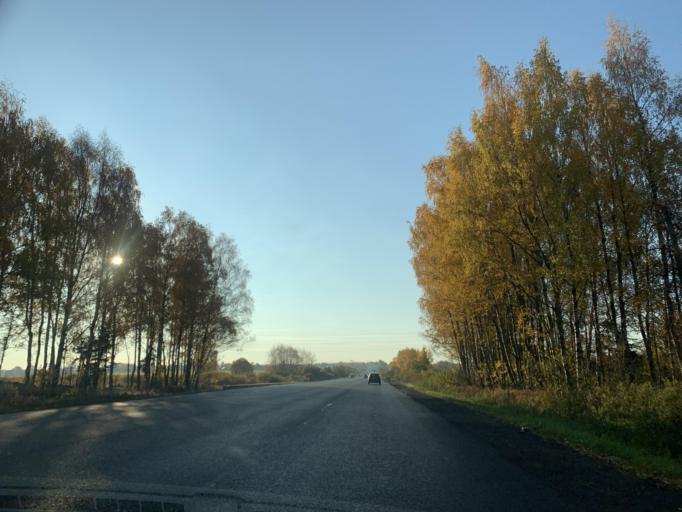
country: RU
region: Jaroslavl
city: Konstantinovskiy
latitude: 57.8013
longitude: 39.5940
